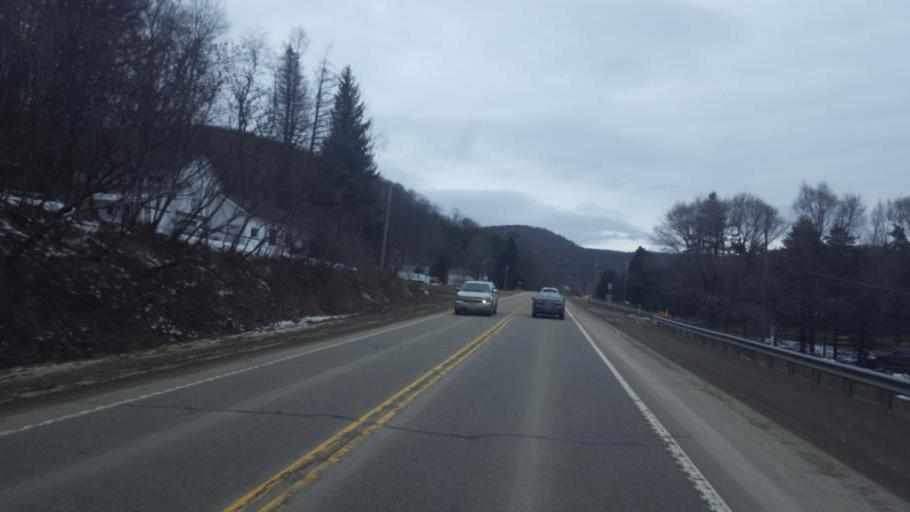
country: US
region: Pennsylvania
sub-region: Potter County
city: Coudersport
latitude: 41.8008
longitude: -78.0153
